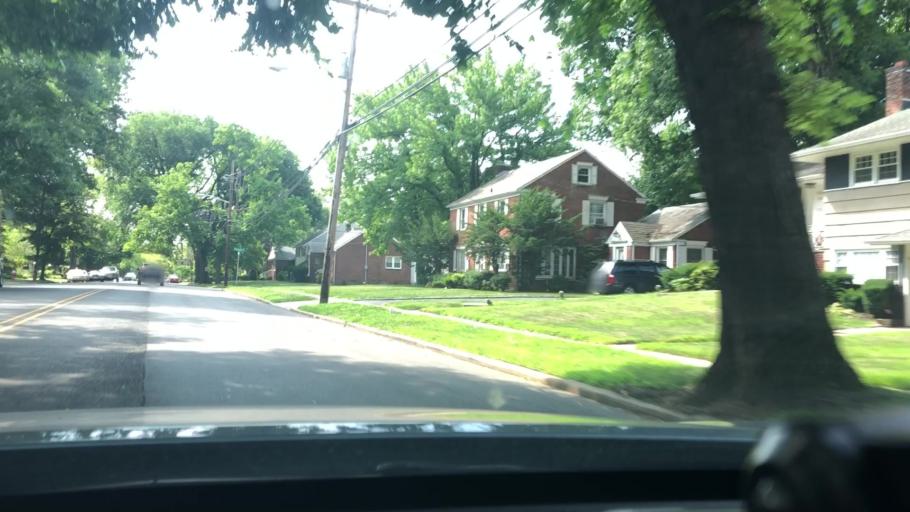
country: US
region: New Jersey
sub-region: Union County
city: Winfield
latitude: 40.6418
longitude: -74.2704
